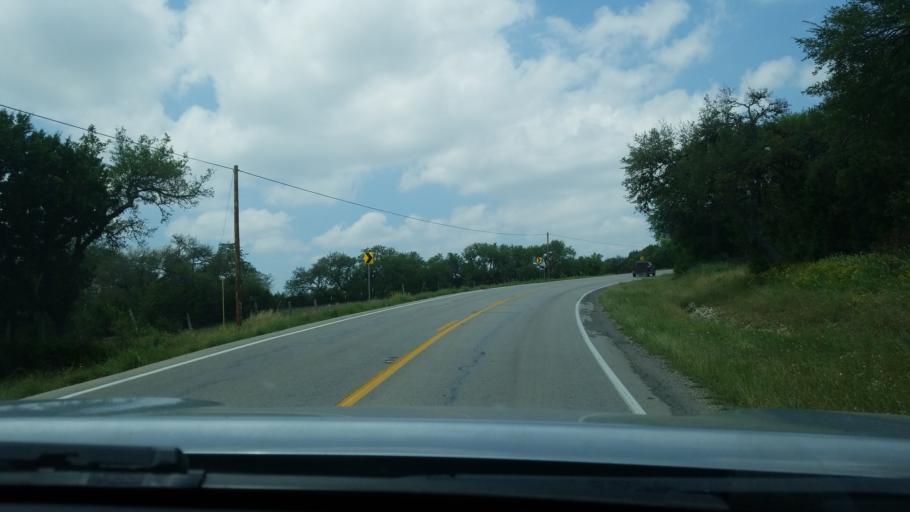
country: US
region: Texas
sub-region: Hays County
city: Dripping Springs
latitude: 30.1537
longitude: -98.0663
